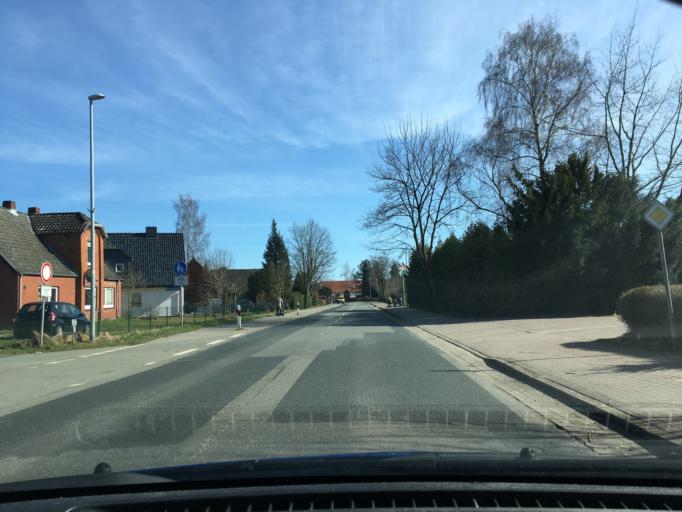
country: DE
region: Lower Saxony
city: Tespe
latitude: 53.3879
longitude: 10.4167
